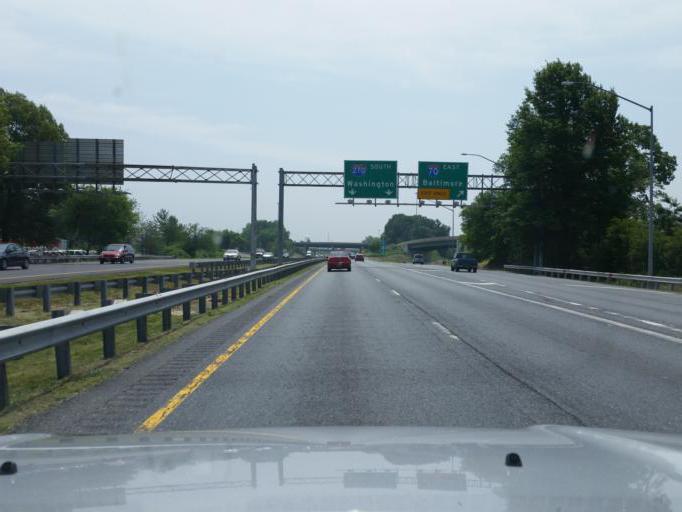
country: US
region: Maryland
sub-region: Frederick County
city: Frederick
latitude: 39.4025
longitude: -77.4293
